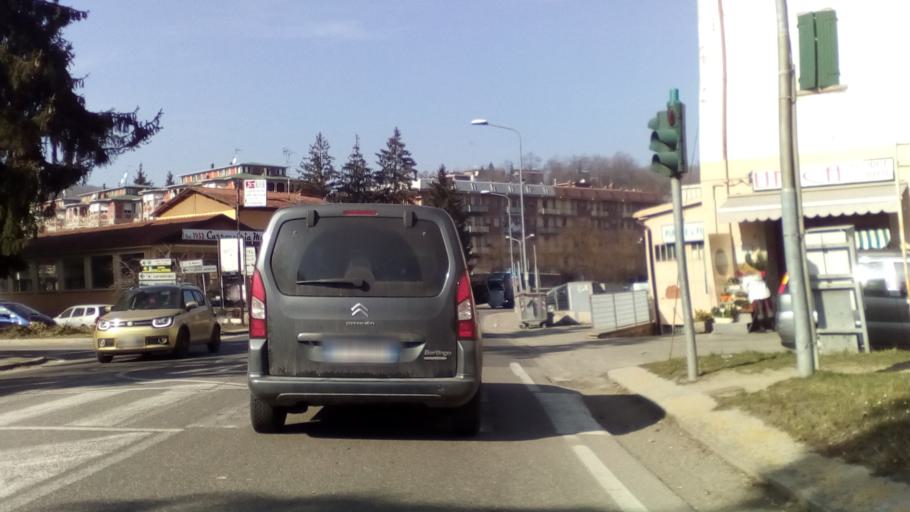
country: IT
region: Emilia-Romagna
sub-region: Provincia di Modena
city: Pavullo nel Frignano
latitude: 44.3311
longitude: 10.8342
